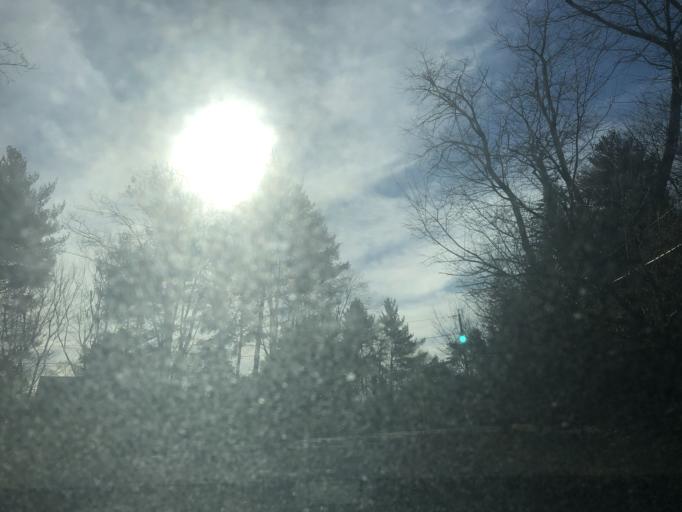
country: US
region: New Jersey
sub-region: Somerset County
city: Kingston
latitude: 40.3633
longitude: -74.6355
